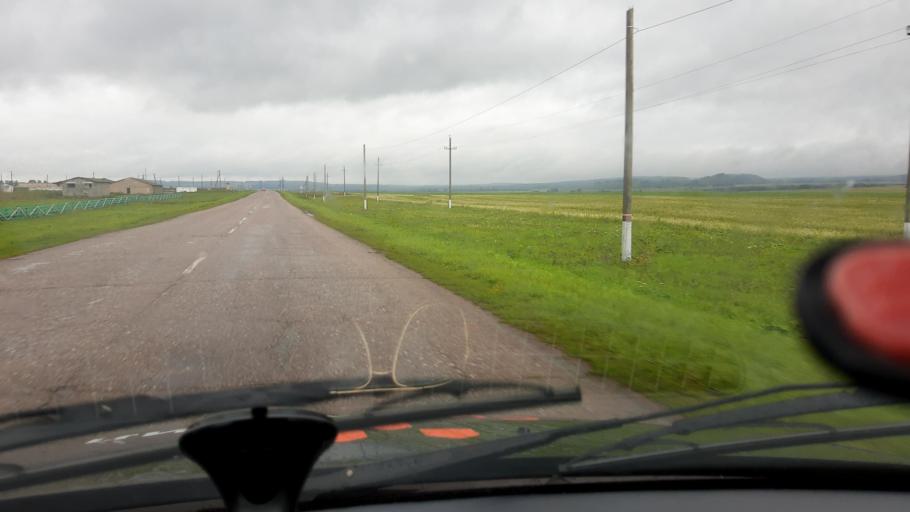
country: RU
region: Bashkortostan
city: Karmaskaly
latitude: 53.9835
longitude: 56.3941
